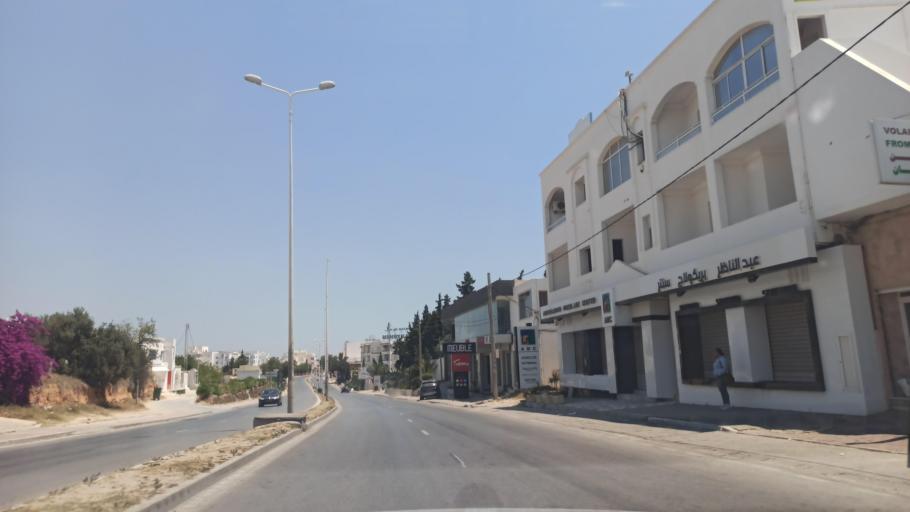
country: TN
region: Nabul
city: Al Hammamat
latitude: 36.4082
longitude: 10.6387
